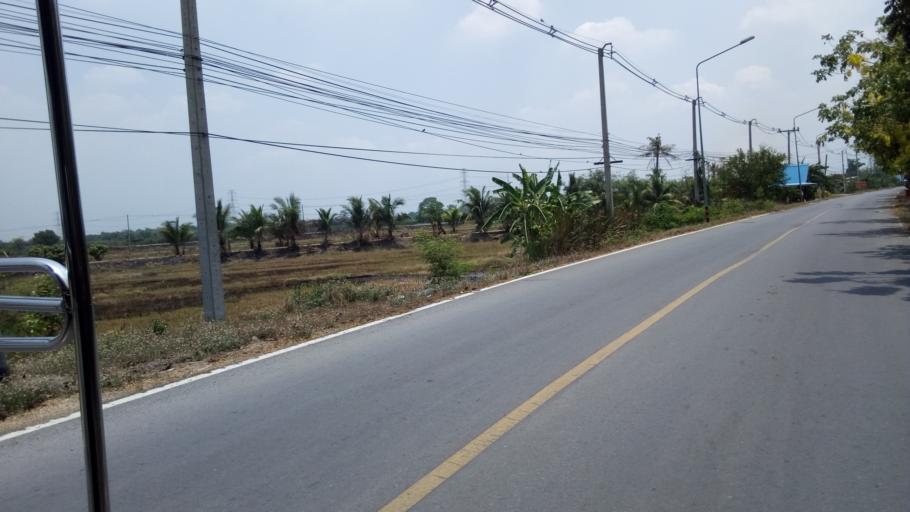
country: TH
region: Pathum Thani
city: Sam Khok
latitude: 14.1108
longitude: 100.5390
